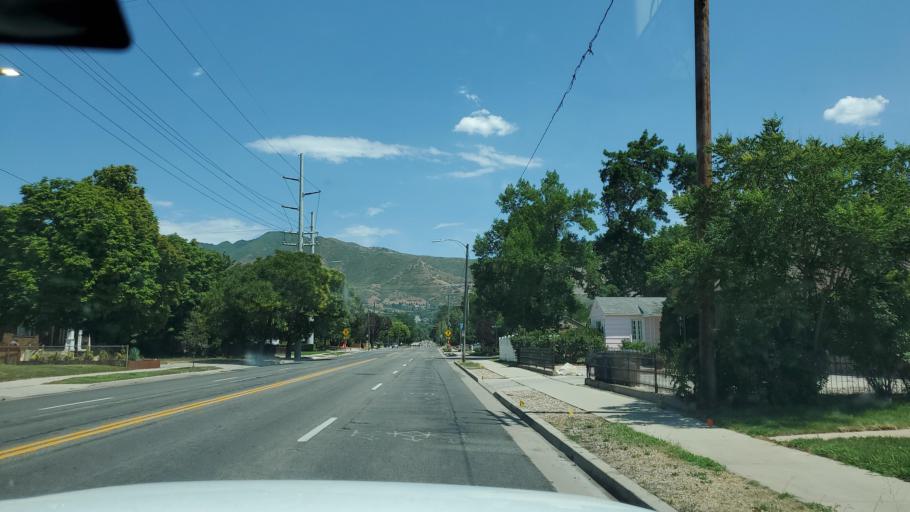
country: US
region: Utah
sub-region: Salt Lake County
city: Willard
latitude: 40.7255
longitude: -111.8380
